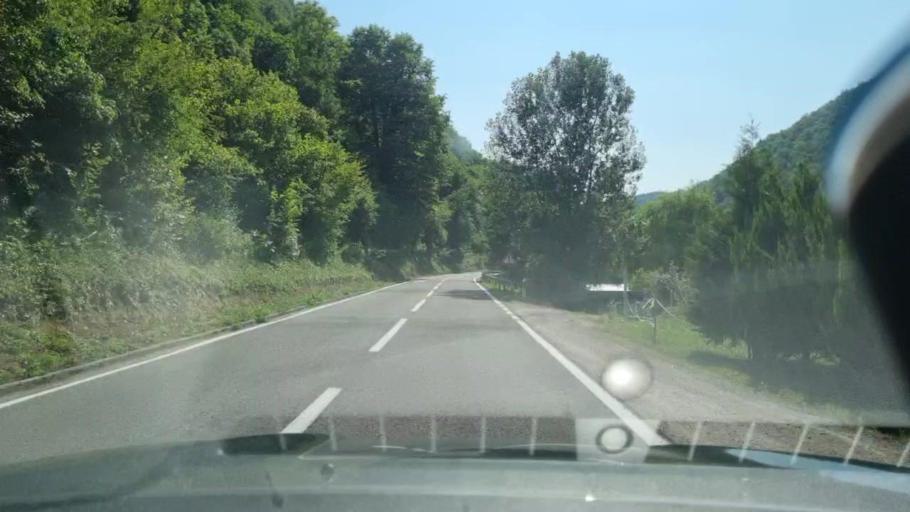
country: BA
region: Federation of Bosnia and Herzegovina
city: Bosanska Krupa
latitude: 44.8747
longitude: 16.1162
